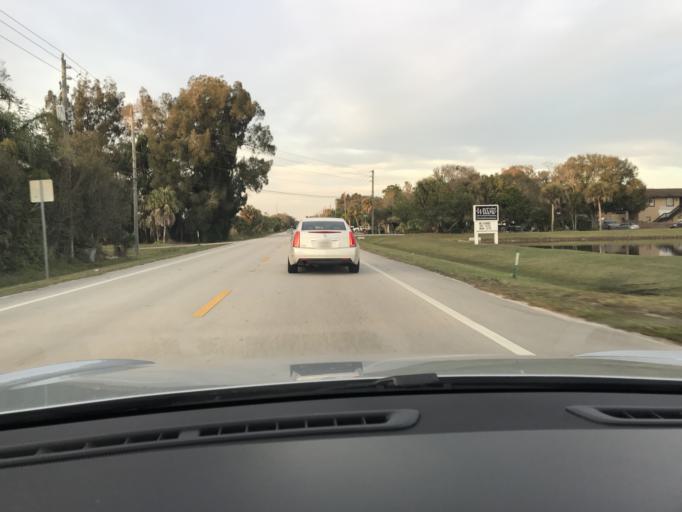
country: US
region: Florida
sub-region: Indian River County
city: Vero Beach South
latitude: 27.6193
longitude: -80.4304
